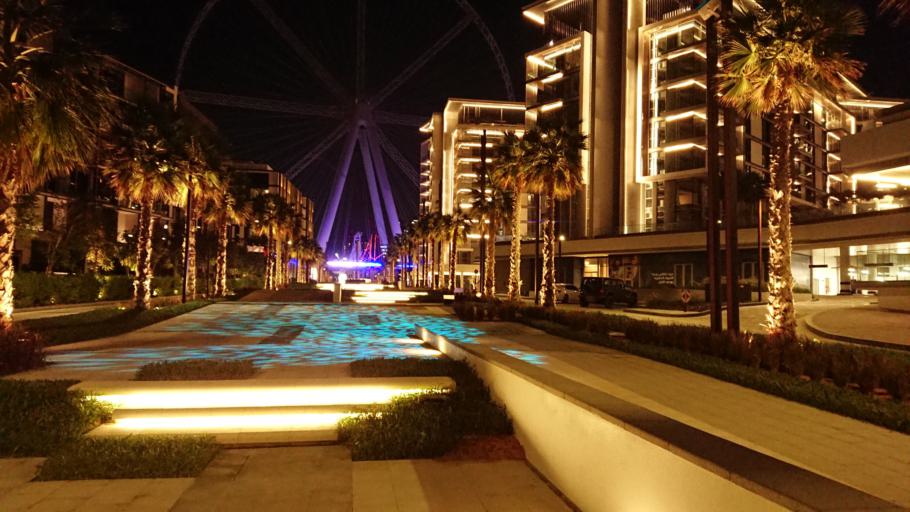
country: AE
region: Dubai
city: Dubai
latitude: 25.0797
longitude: 55.1196
